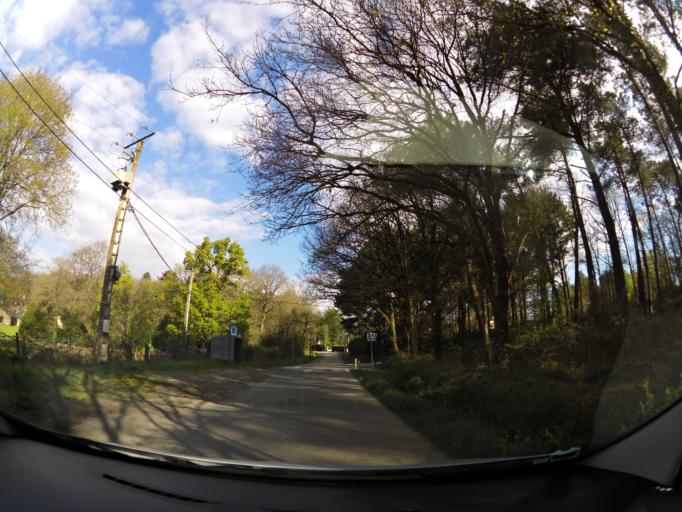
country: FR
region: Brittany
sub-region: Departement d'Ille-et-Vilaine
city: Laille
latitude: 47.9687
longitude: -1.7082
